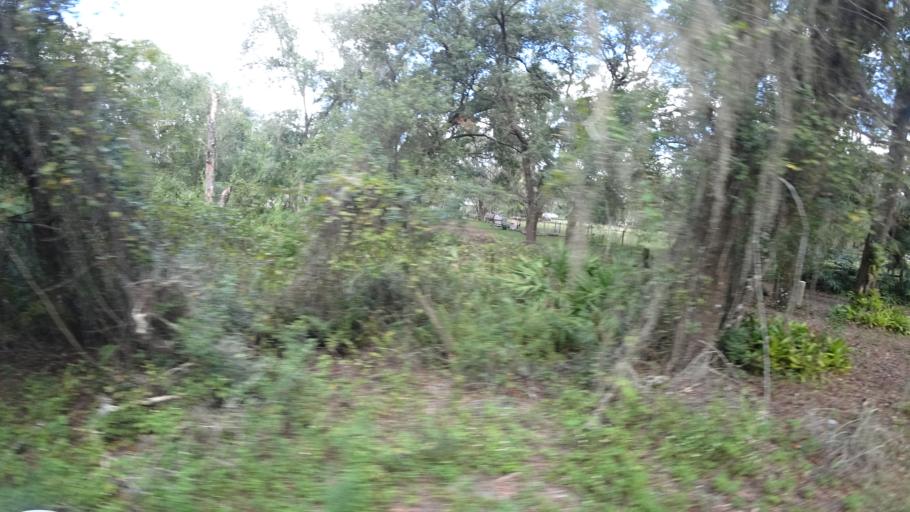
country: US
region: Florida
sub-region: Sarasota County
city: Lake Sarasota
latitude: 27.3274
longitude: -82.2678
